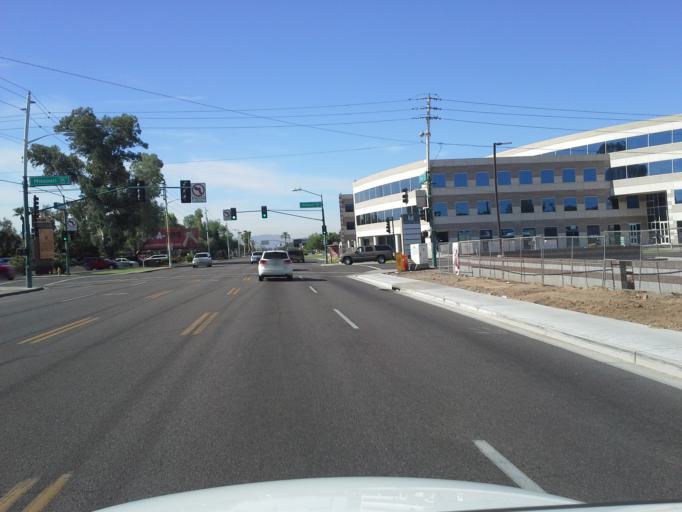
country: US
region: Arizona
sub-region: Maricopa County
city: Phoenix
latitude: 33.5170
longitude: -112.0651
